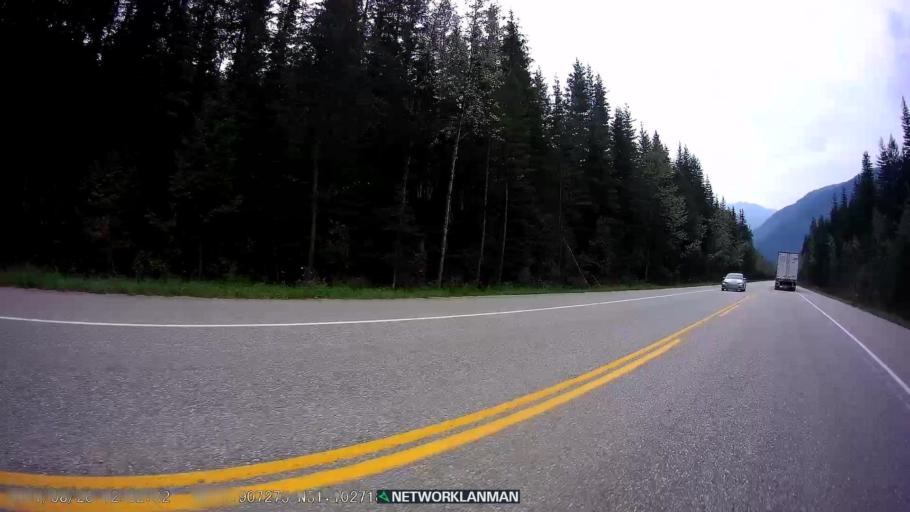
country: CA
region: British Columbia
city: Revelstoke
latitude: 51.1031
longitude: -117.9080
